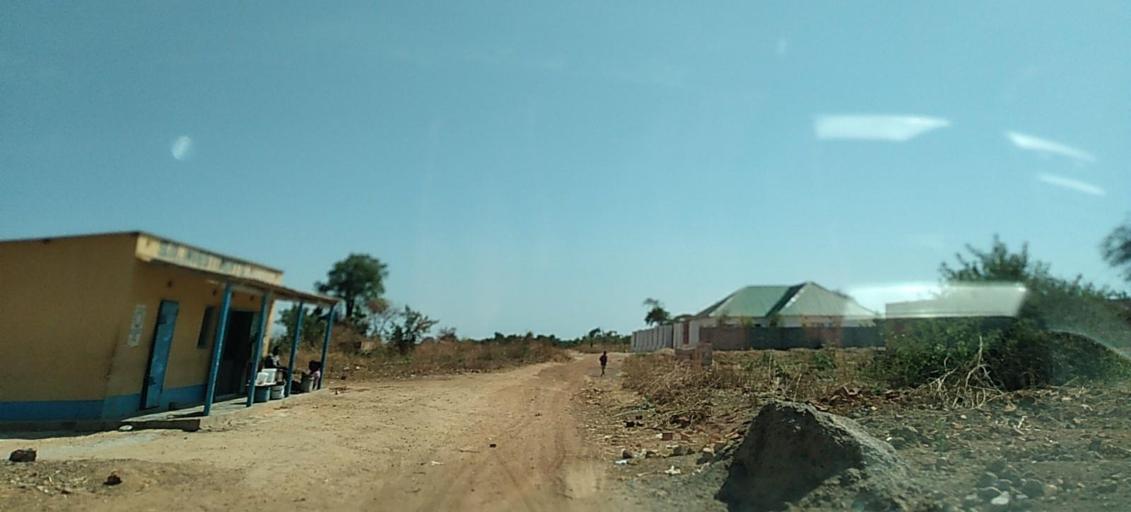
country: ZM
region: Copperbelt
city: Chililabombwe
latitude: -12.3180
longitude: 27.8627
